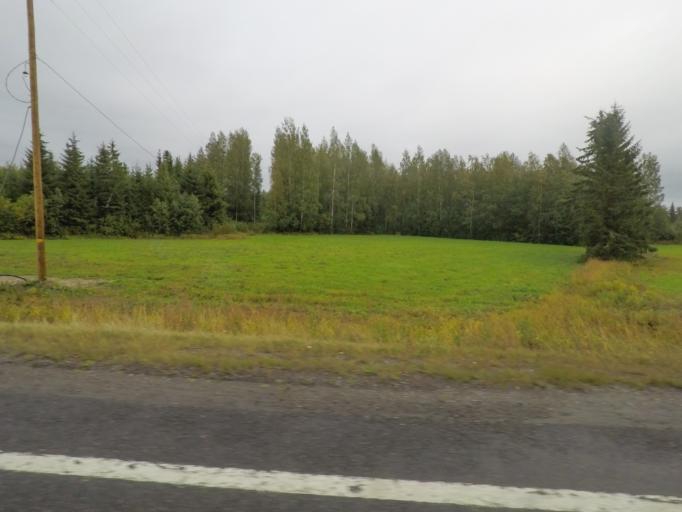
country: FI
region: Southern Savonia
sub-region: Pieksaemaeki
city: Joroinen
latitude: 62.1324
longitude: 27.8388
